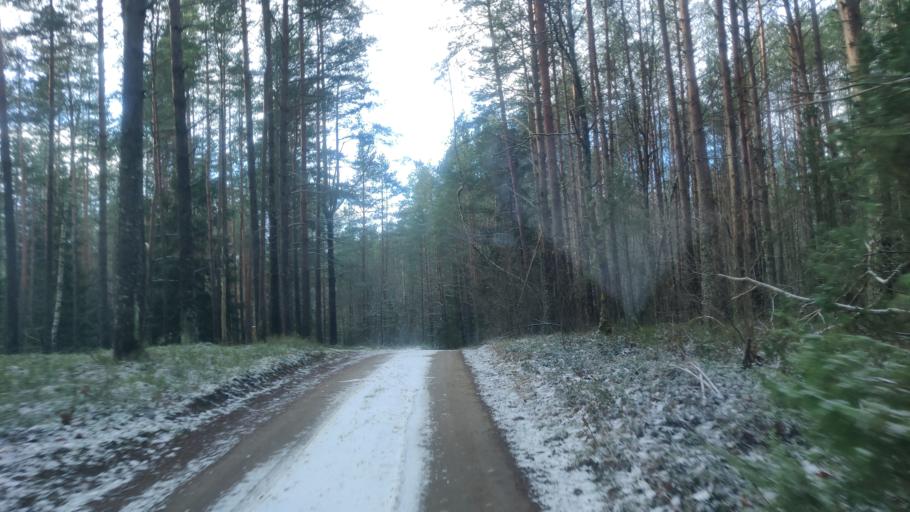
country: LT
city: Trakai
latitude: 54.5668
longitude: 24.9208
